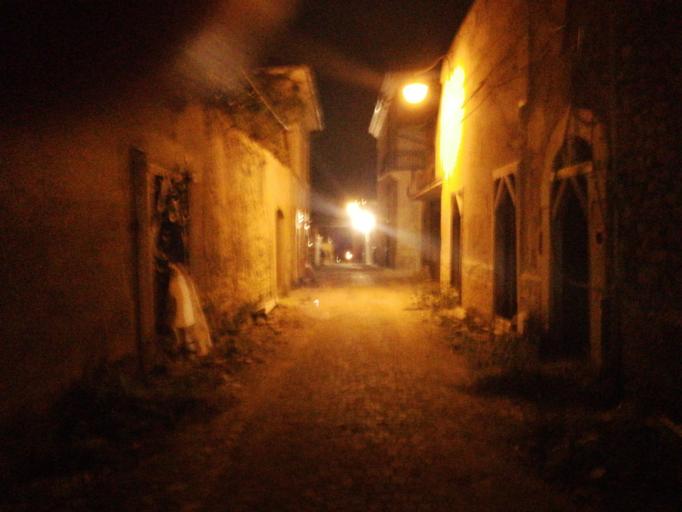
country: IT
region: Abruzzo
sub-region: Provincia dell' Aquila
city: L'Aquila
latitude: 42.3522
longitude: 13.3955
